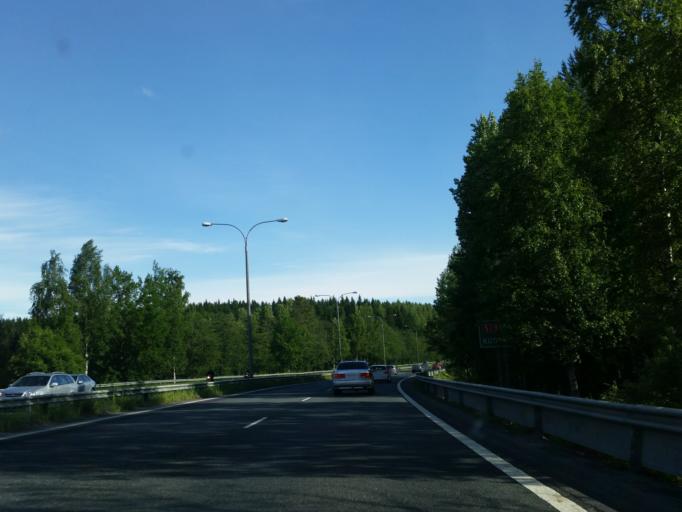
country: FI
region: Northern Savo
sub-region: Kuopio
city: Kuopio
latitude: 62.9293
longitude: 27.6745
